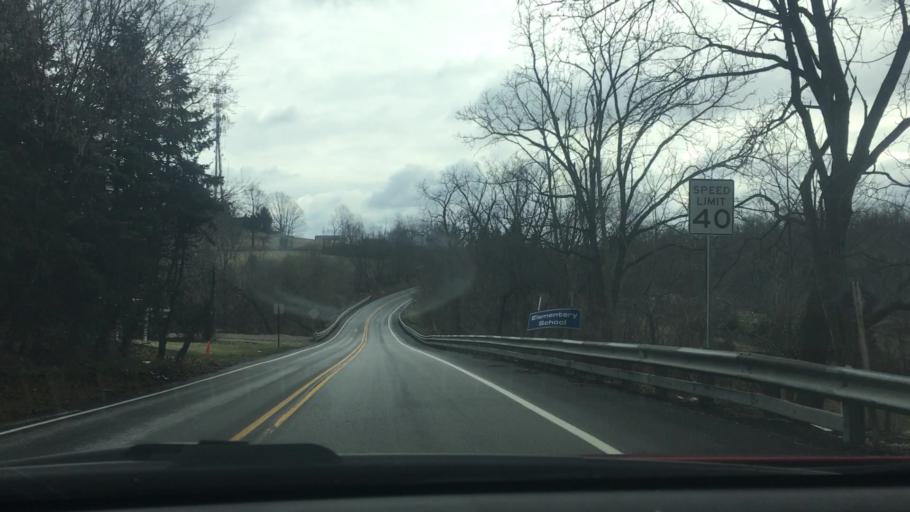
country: US
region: Pennsylvania
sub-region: Allegheny County
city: Oakdale
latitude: 40.3842
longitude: -80.1848
